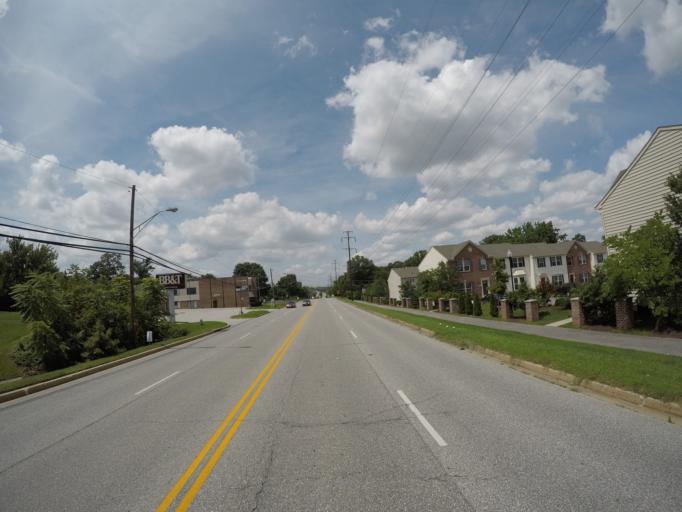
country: US
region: Maryland
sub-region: Anne Arundel County
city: Odenton
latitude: 39.0834
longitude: -76.6925
